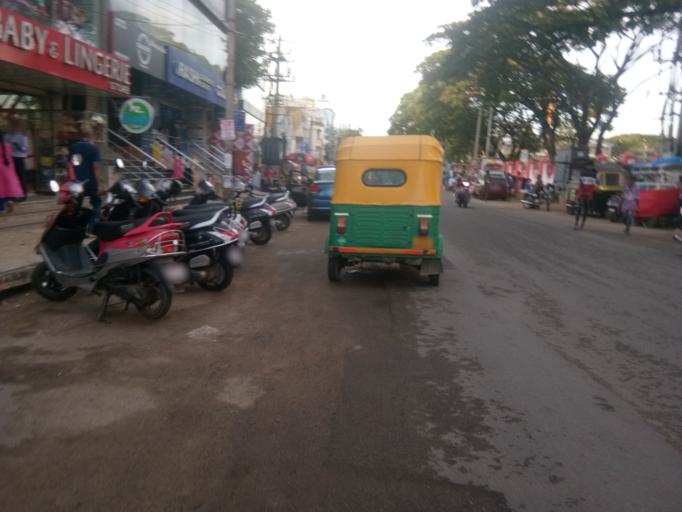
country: IN
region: Karnataka
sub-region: Bangalore Urban
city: Bangalore
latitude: 13.0178
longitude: 77.6367
